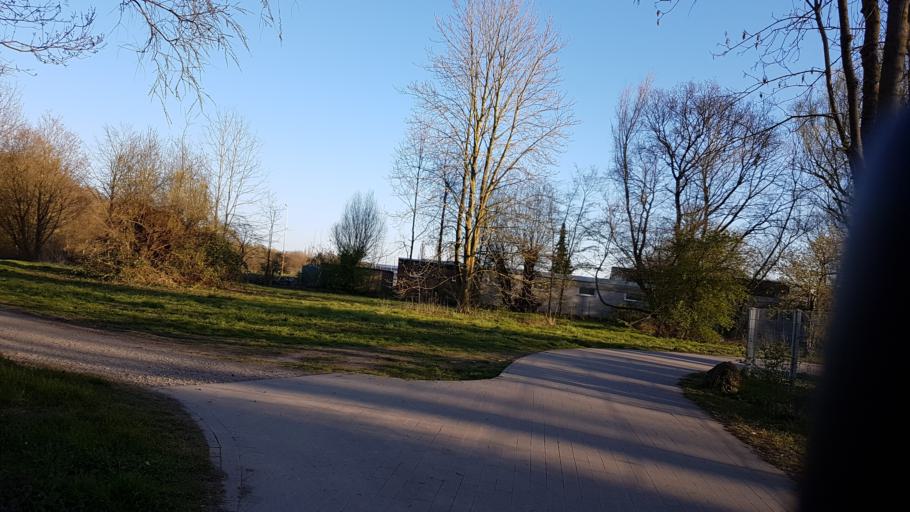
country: DE
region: Lower Saxony
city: Hemmingen
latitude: 52.3313
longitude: 9.7407
